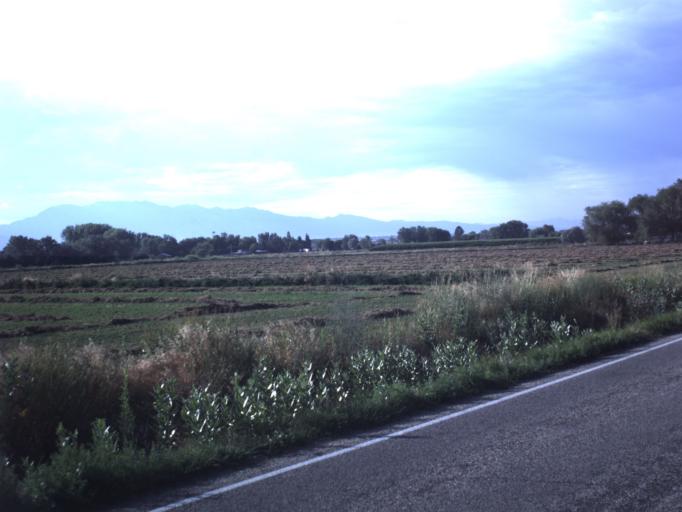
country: US
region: Utah
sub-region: Weber County
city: West Haven
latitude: 41.2403
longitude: -112.0927
